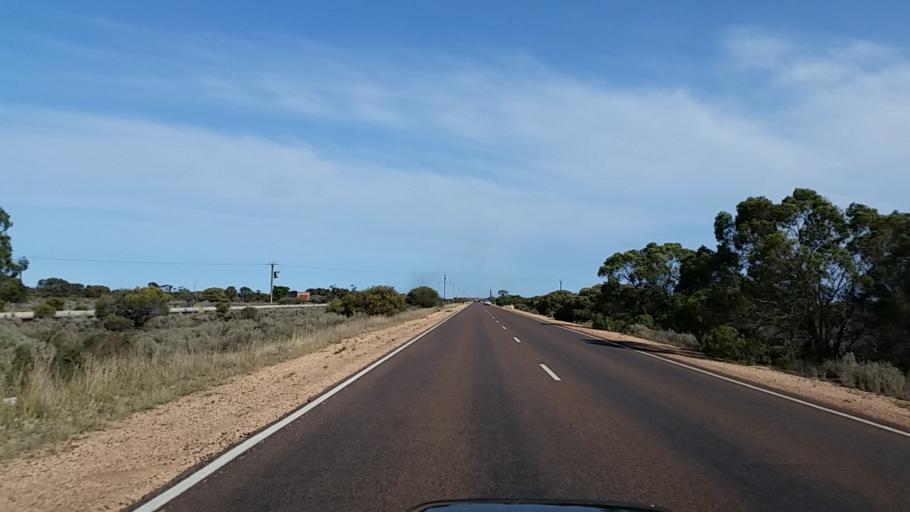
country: AU
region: South Australia
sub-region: Whyalla
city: Whyalla
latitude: -32.9661
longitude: 137.5781
